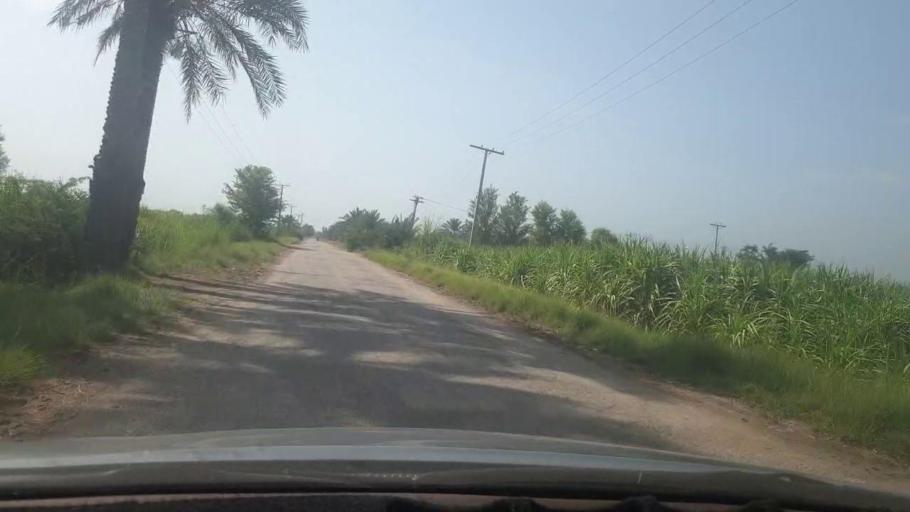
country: PK
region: Sindh
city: Gambat
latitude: 27.3251
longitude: 68.5529
